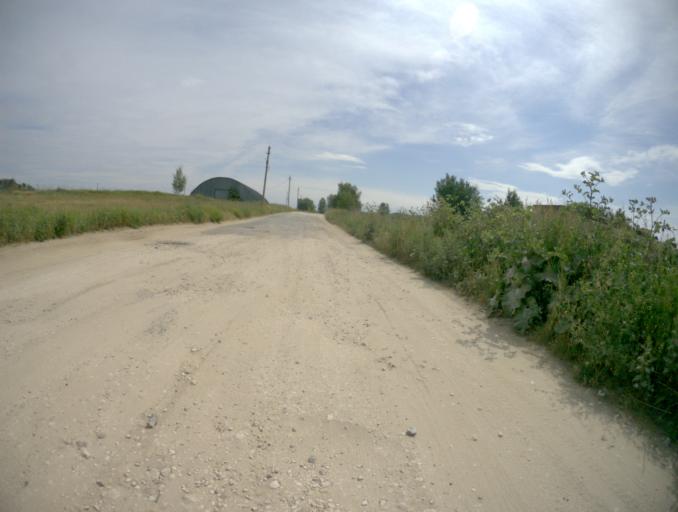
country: RU
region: Vladimir
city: Raduzhnyy
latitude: 56.0273
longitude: 40.3059
